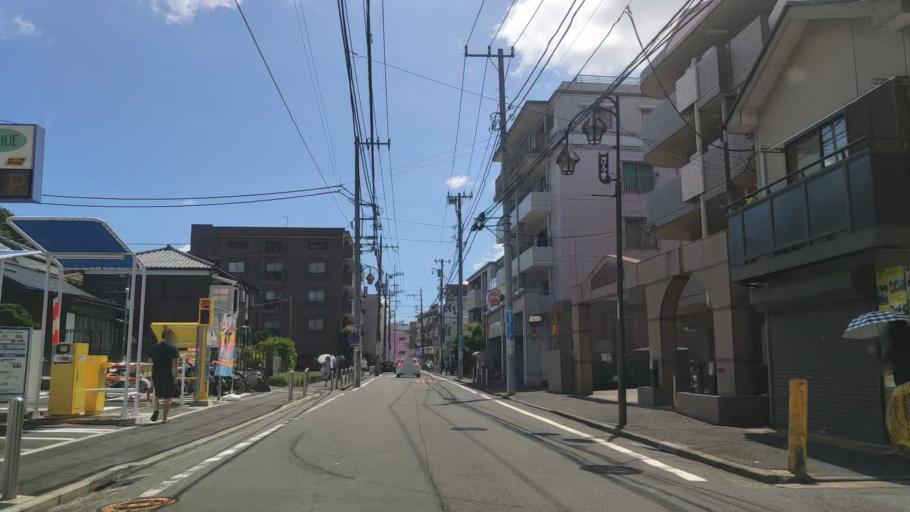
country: JP
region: Kanagawa
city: Yokohama
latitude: 35.5235
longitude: 139.6258
